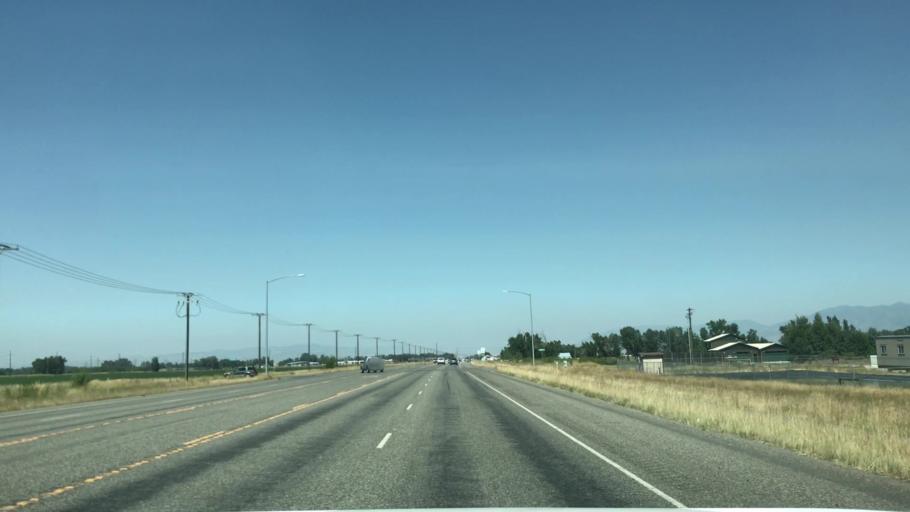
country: US
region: Montana
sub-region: Gallatin County
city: Four Corners
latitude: 45.6844
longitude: -111.1858
